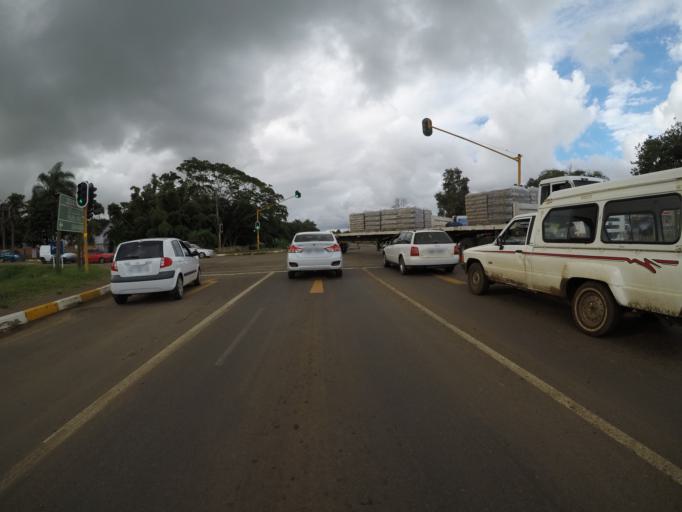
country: ZA
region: KwaZulu-Natal
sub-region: uMkhanyakude District Municipality
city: Mtubatuba
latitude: -28.4145
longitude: 32.1840
